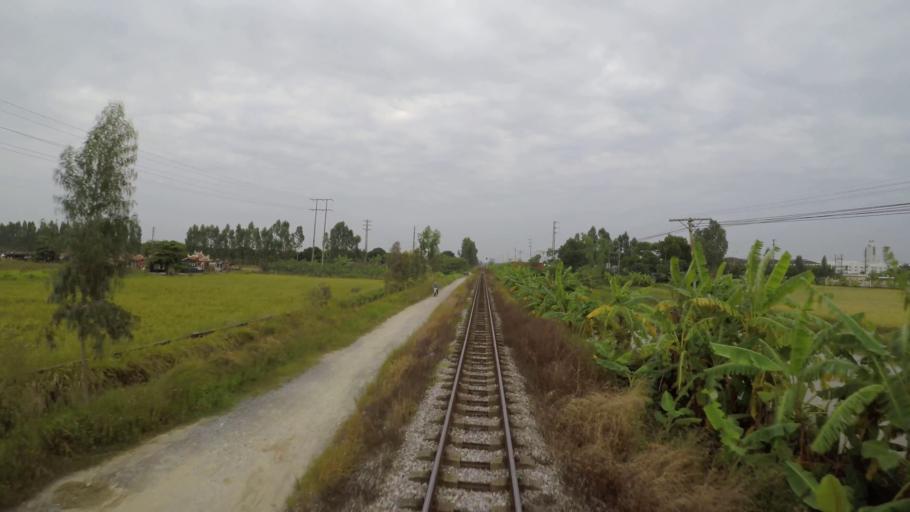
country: VN
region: Hai Duong
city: Lai Cach
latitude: 20.9475
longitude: 106.2589
